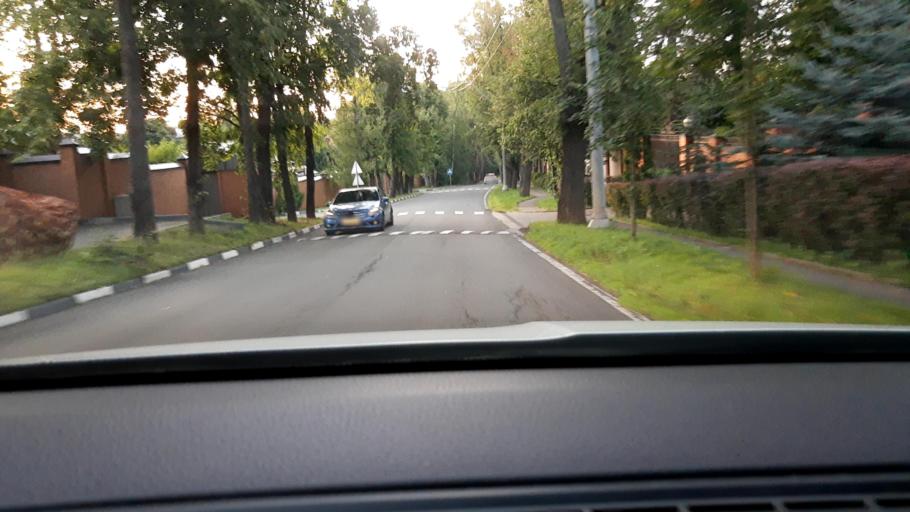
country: RU
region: Moskovskaya
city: Zarech'ye
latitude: 55.6885
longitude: 37.3831
